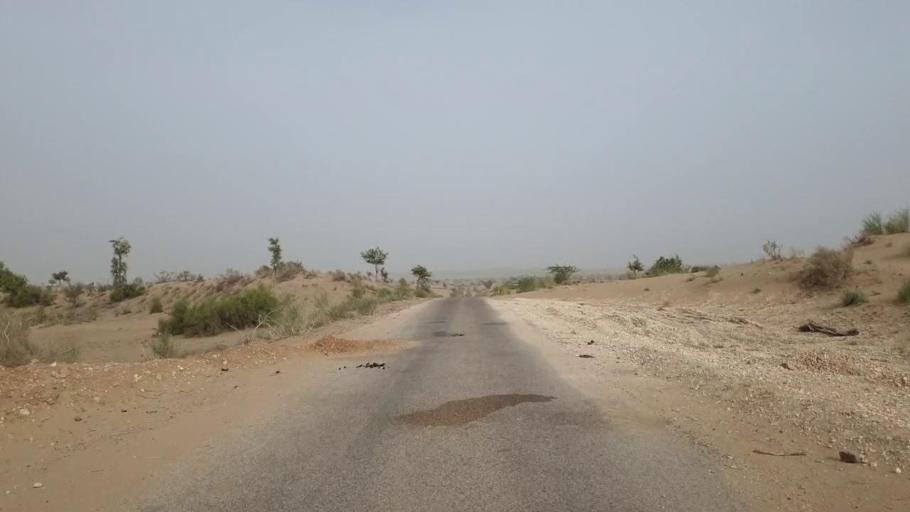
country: PK
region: Sindh
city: Islamkot
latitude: 24.5556
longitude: 70.3486
